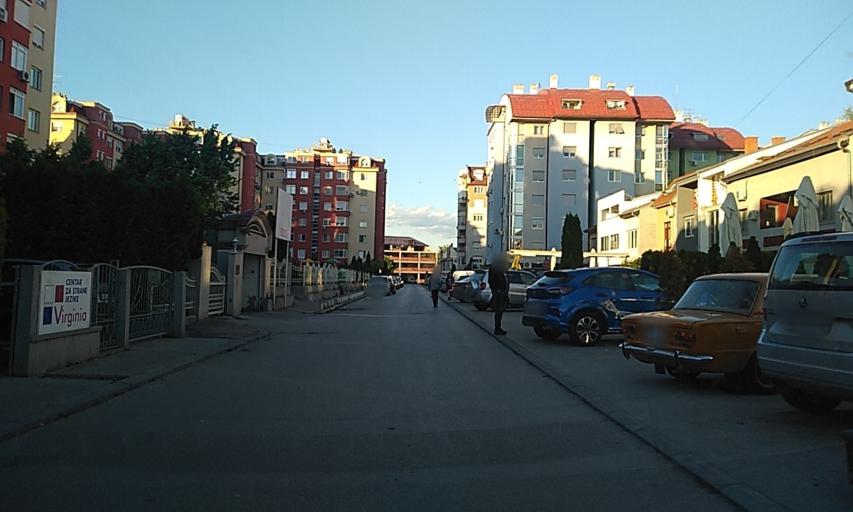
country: RS
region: Central Serbia
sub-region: Nisavski Okrug
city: Nis
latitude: 43.3223
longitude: 21.9294
